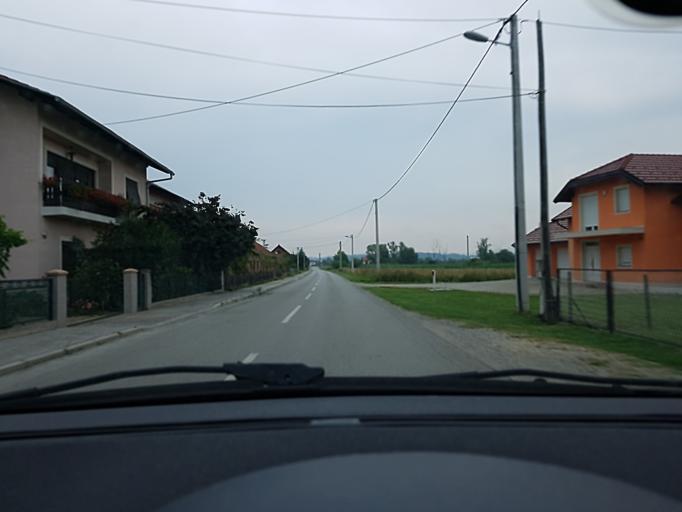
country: HR
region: Zagrebacka
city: Jakovlje
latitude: 45.9845
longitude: 15.8398
